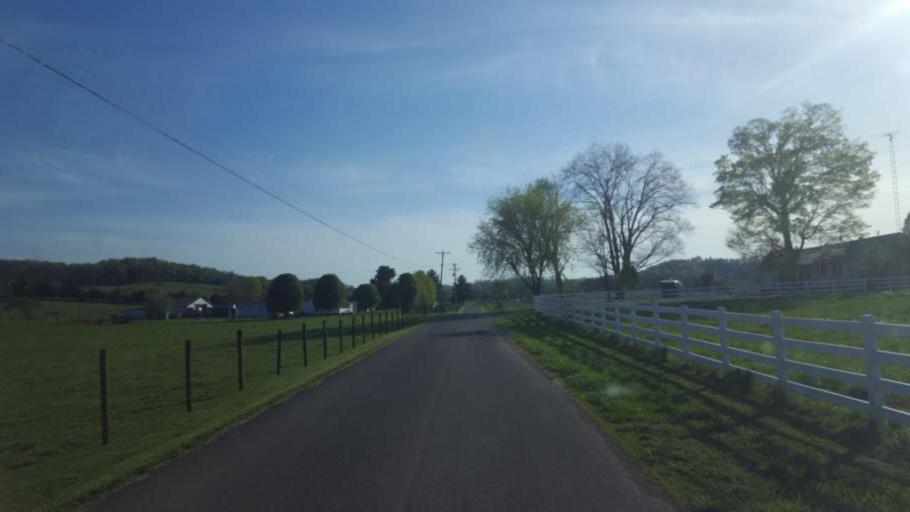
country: US
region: Kentucky
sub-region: Barren County
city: Cave City
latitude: 37.1573
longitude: -85.9736
